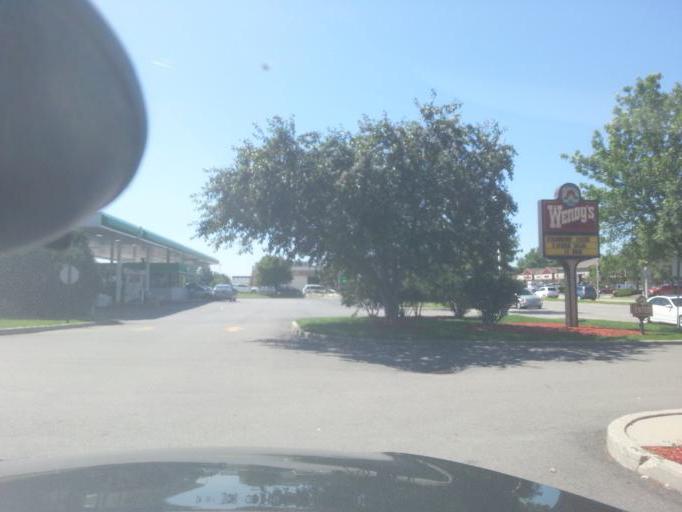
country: US
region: Wisconsin
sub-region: Dane County
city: Middleton
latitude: 43.0511
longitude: -89.5028
